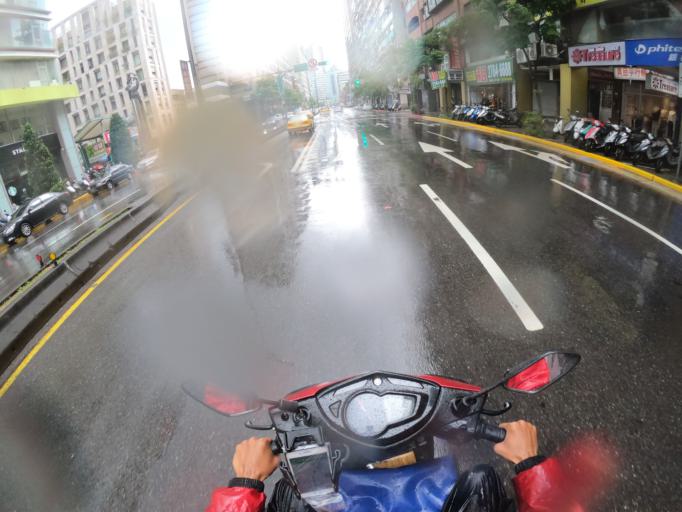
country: TW
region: Taipei
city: Taipei
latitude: 25.0406
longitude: 121.5732
